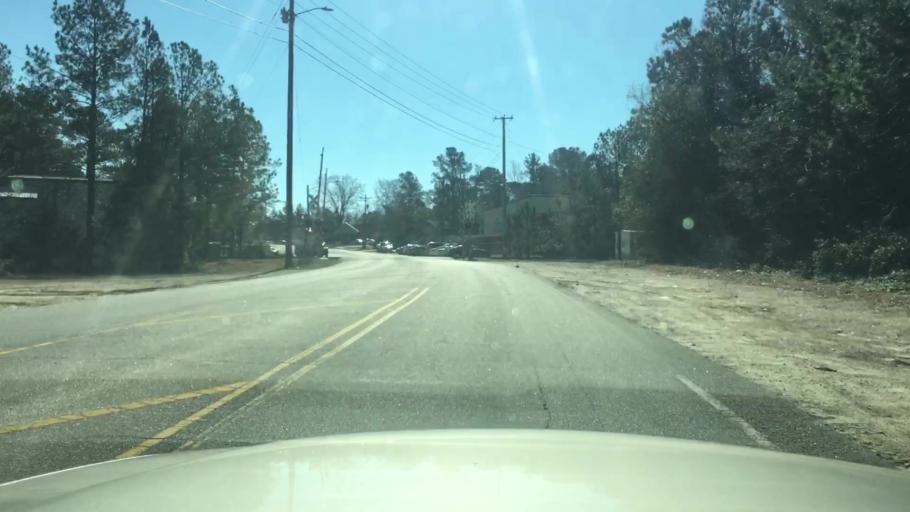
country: US
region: North Carolina
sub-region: Cumberland County
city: Fayetteville
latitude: 35.0386
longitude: -78.8965
